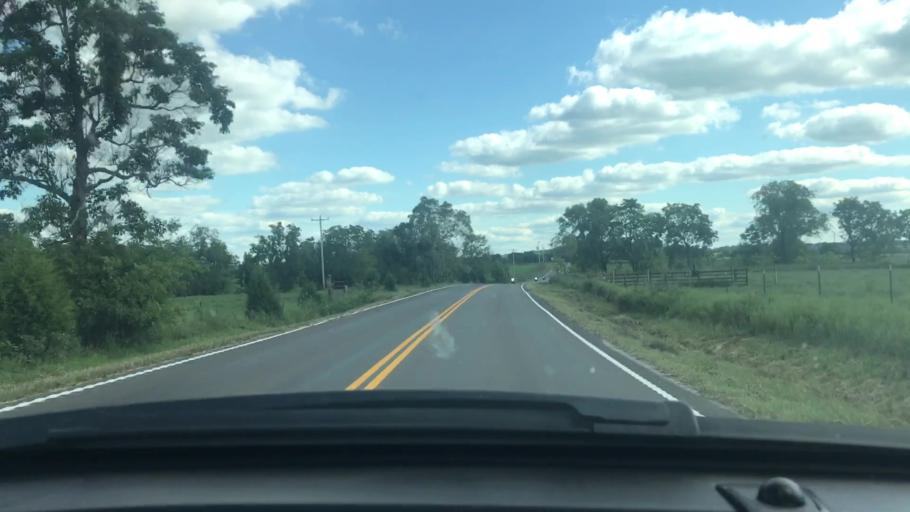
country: US
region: Missouri
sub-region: Wright County
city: Mountain Grove
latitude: 37.2950
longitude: -92.3087
